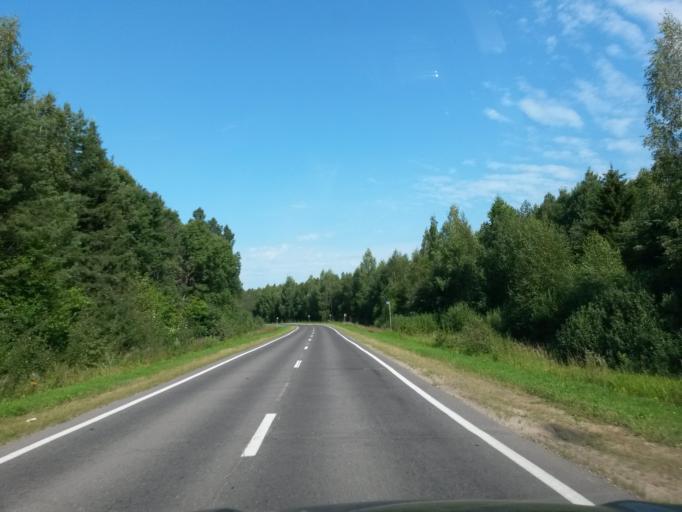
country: RU
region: Jaroslavl
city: Konstantinovskiy
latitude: 57.8558
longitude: 39.6206
